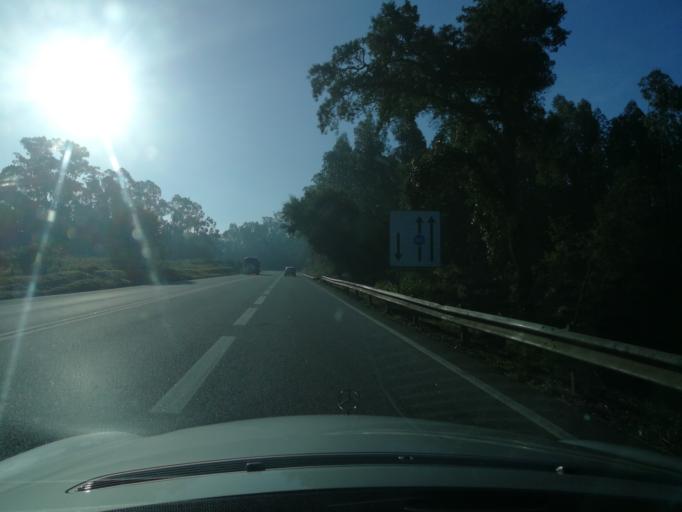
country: PT
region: Aveiro
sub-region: Agueda
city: Valongo
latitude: 40.6278
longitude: -8.4647
